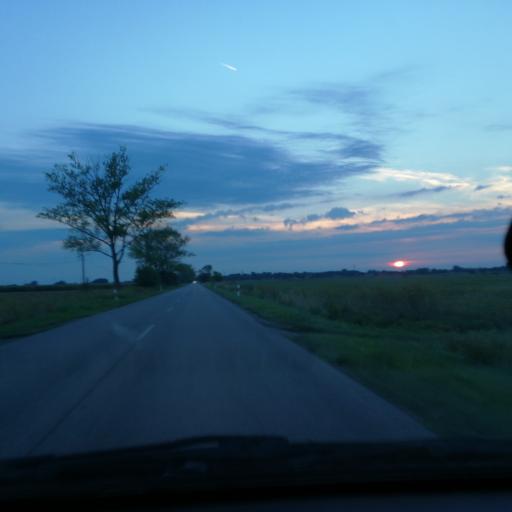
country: HU
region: Bacs-Kiskun
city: Kalocsa
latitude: 46.5092
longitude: 19.0727
